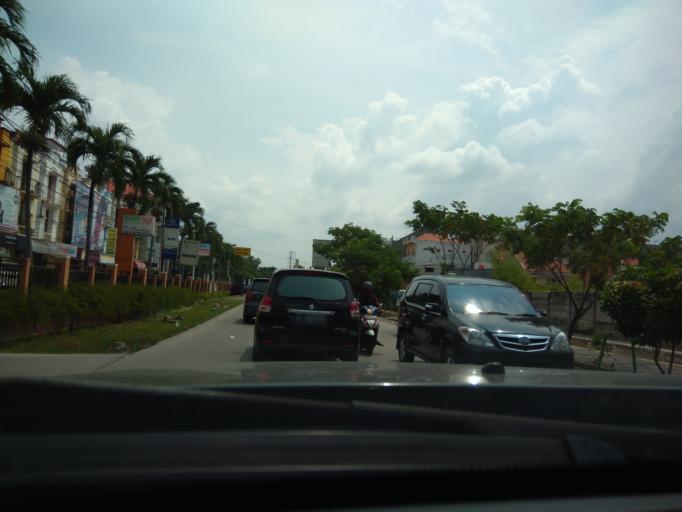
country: ID
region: West Java
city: Bekasi
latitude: -6.1832
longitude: 106.9786
